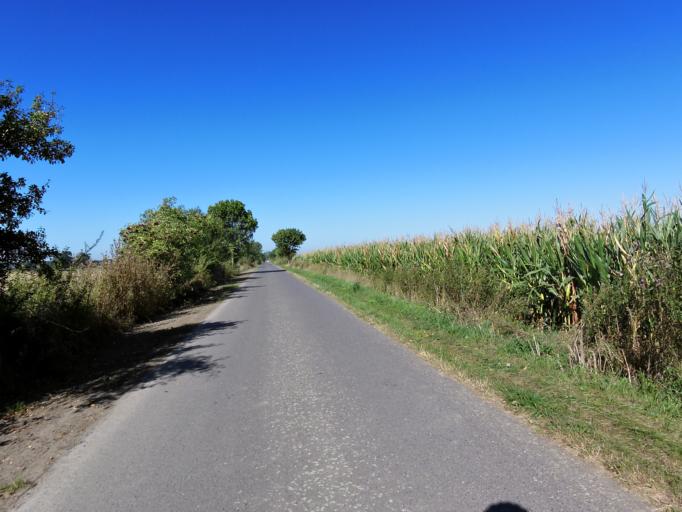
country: DE
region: Saxony
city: Elsnig
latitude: 51.6153
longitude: 12.9552
